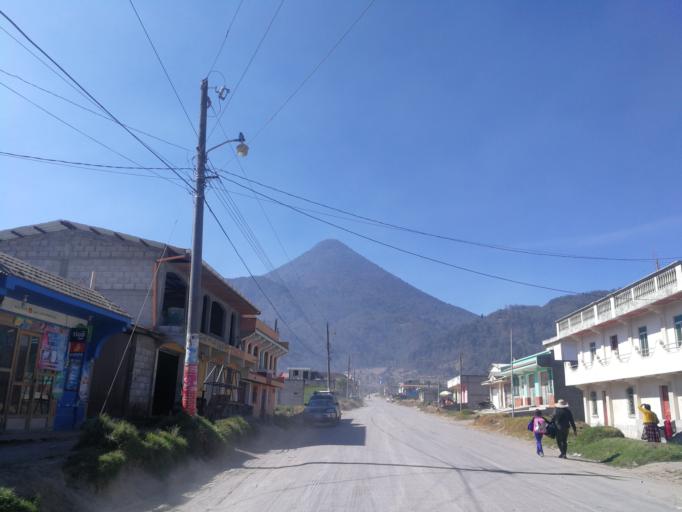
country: GT
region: Quetzaltenango
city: Quetzaltenango
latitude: 14.7955
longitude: -91.5464
